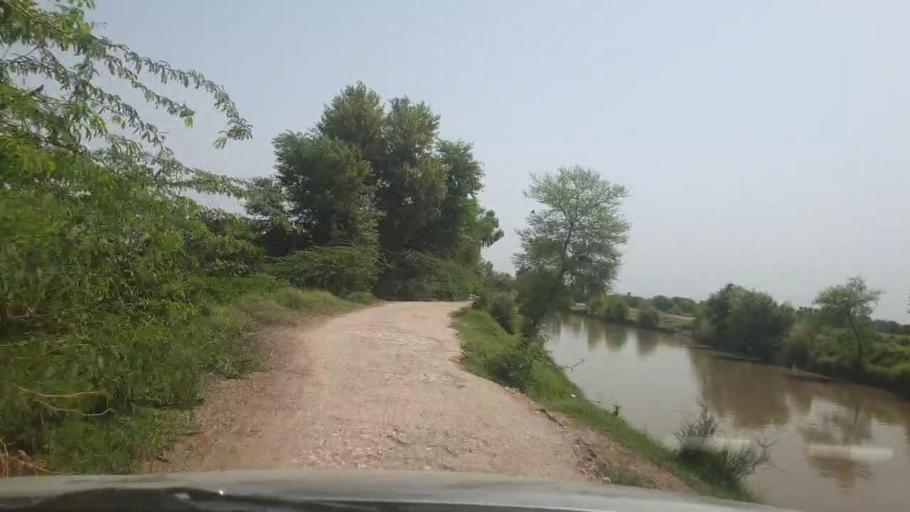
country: PK
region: Sindh
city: Pano Aqil
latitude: 27.8975
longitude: 69.1433
